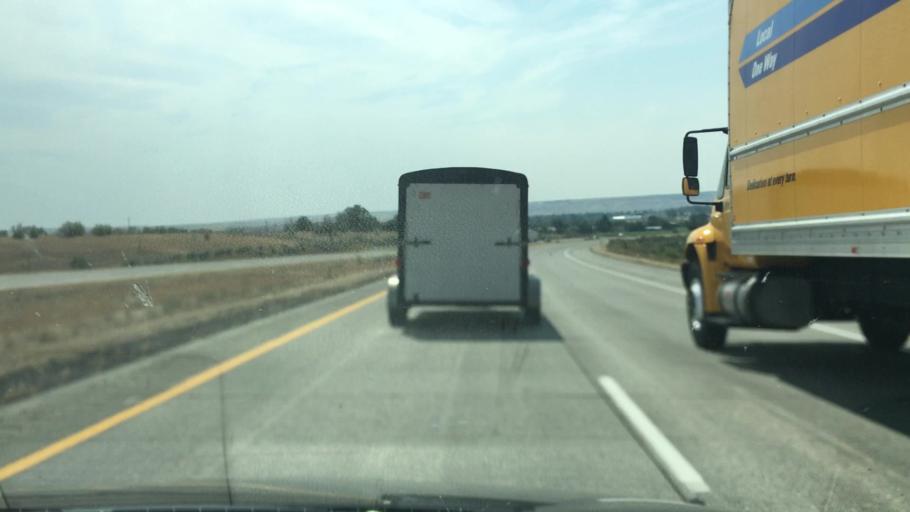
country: US
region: Idaho
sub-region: Elmore County
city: Glenns Ferry
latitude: 42.9629
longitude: -115.2587
